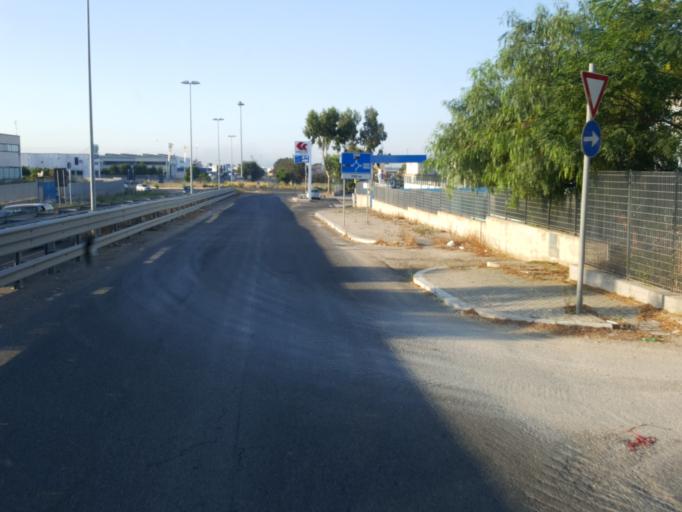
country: IT
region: Latium
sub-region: Citta metropolitana di Roma Capitale
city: Aurelia
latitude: 42.1217
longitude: 11.7782
